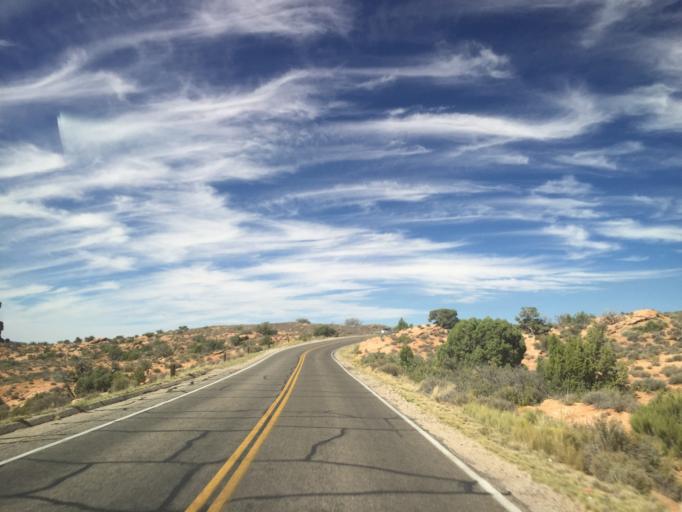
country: US
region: Utah
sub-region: Grand County
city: Moab
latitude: 38.6939
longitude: -109.5492
